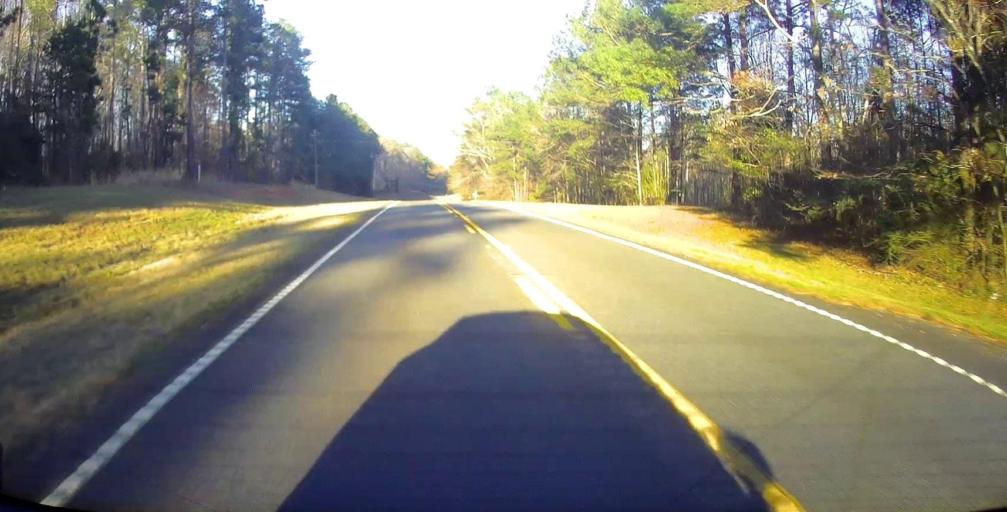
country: US
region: Georgia
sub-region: Talbot County
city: Talbotton
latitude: 32.6620
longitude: -84.6336
